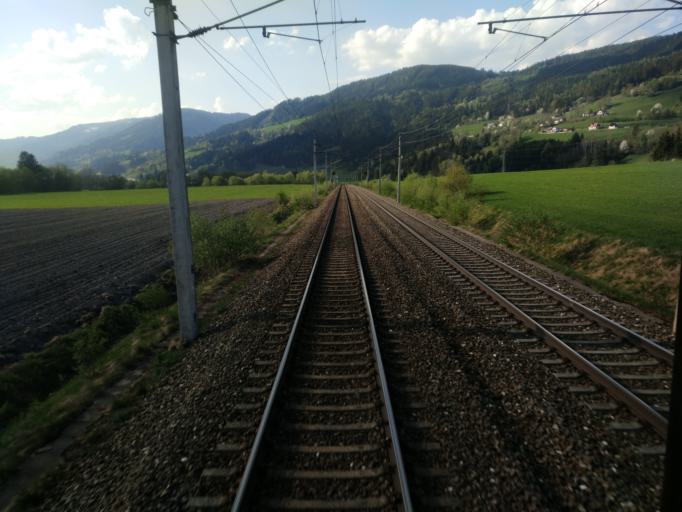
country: AT
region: Styria
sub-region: Politischer Bezirk Liezen
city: Trieben
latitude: 47.4989
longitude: 14.4722
